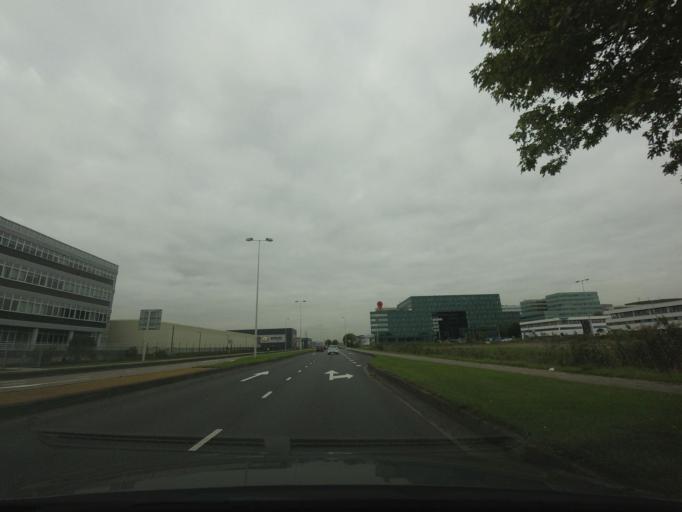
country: NL
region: North Holland
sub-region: Gemeente Ouder-Amstel
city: Duivendrecht
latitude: 52.3046
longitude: 4.9430
